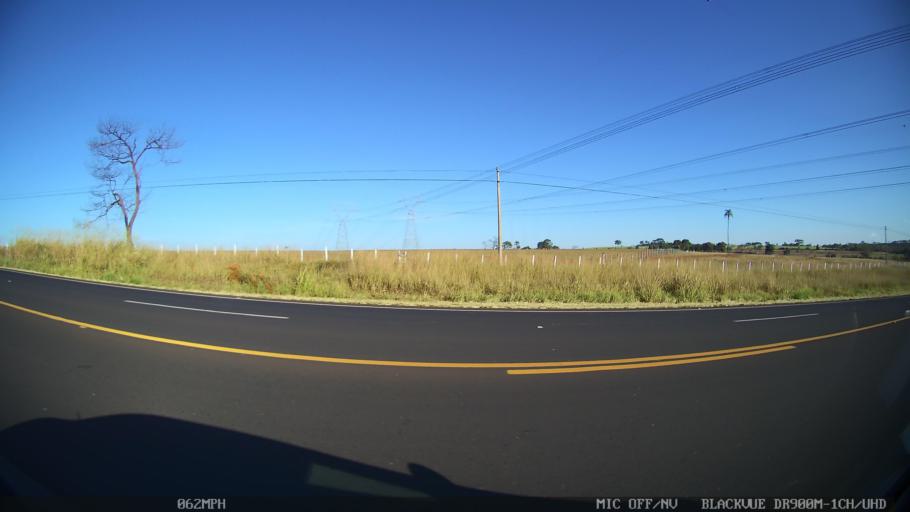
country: BR
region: Sao Paulo
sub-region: Olimpia
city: Olimpia
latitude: -20.7078
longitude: -48.9644
